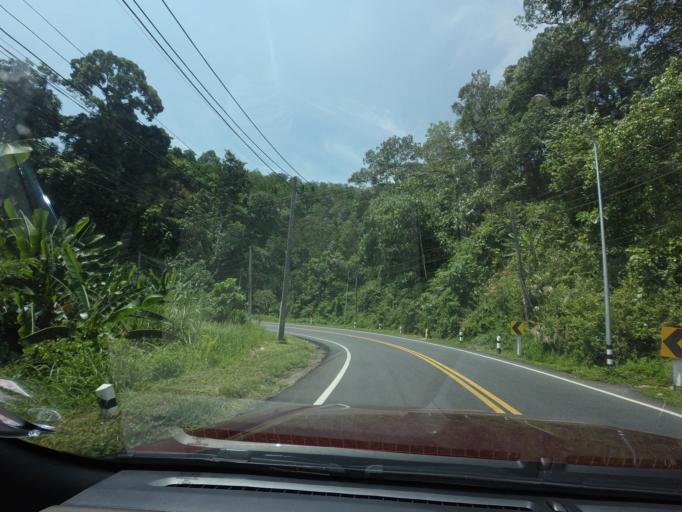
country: TH
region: Yala
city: Betong
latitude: 5.9074
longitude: 101.1506
